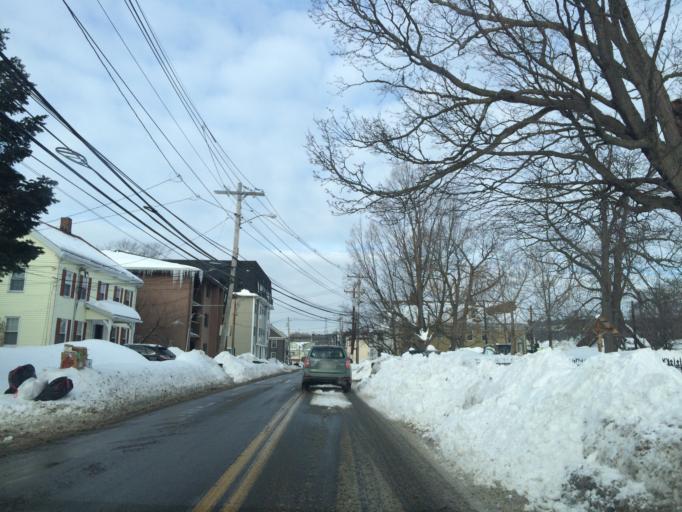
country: US
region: Massachusetts
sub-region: Middlesex County
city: Waltham
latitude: 42.3780
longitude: -71.2371
